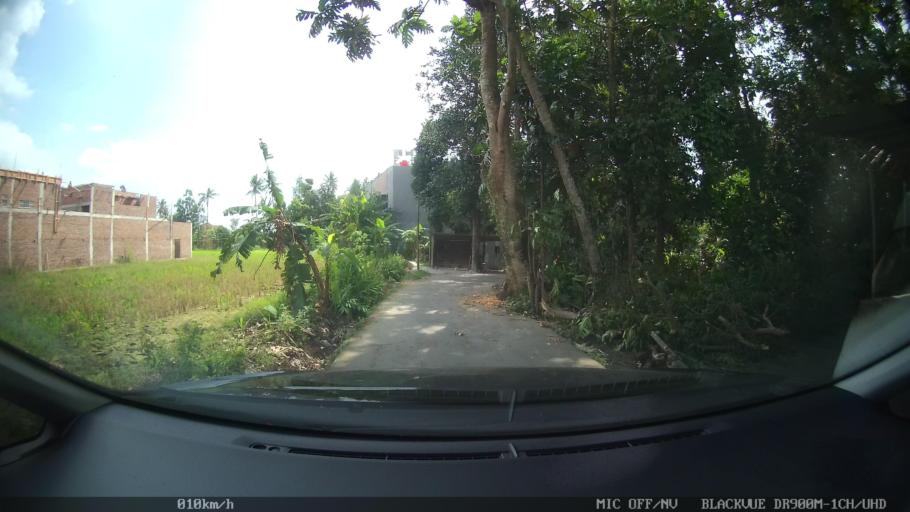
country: ID
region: Daerah Istimewa Yogyakarta
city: Kasihan
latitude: -7.8135
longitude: 110.3305
